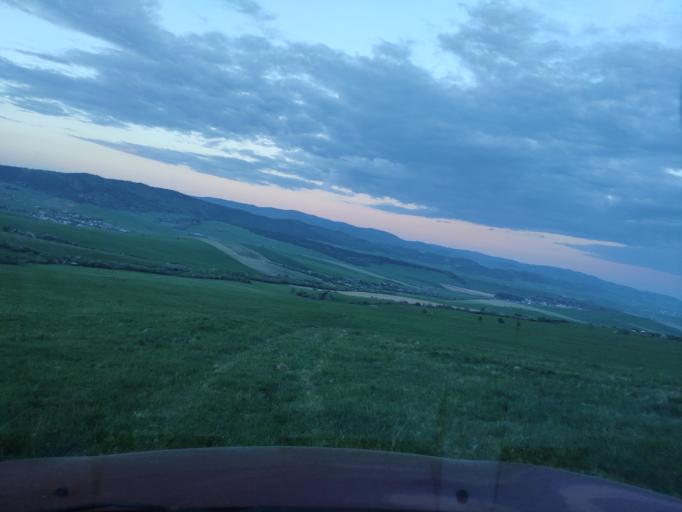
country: SK
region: Presovsky
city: Lipany
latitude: 49.1758
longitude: 20.8039
